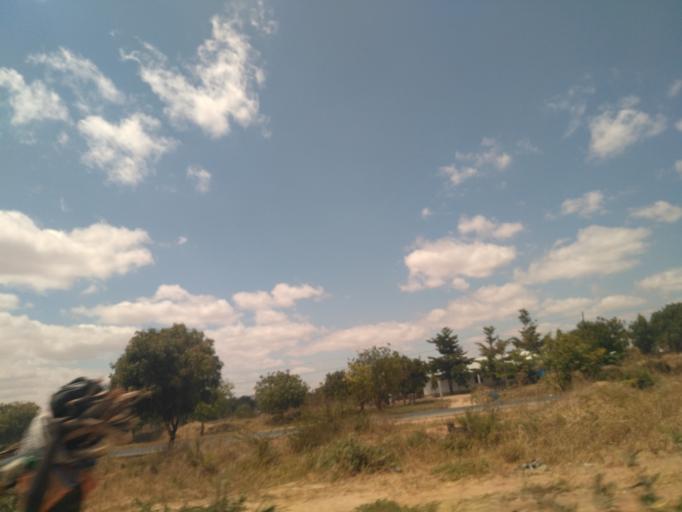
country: TZ
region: Dodoma
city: Kisasa
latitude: -6.1607
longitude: 35.7934
